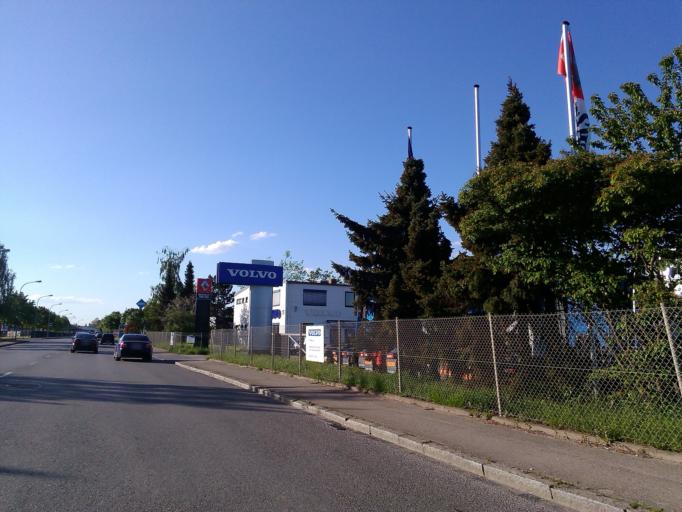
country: DE
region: Bavaria
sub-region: Swabia
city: Augsburg
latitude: 48.3913
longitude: 10.9344
